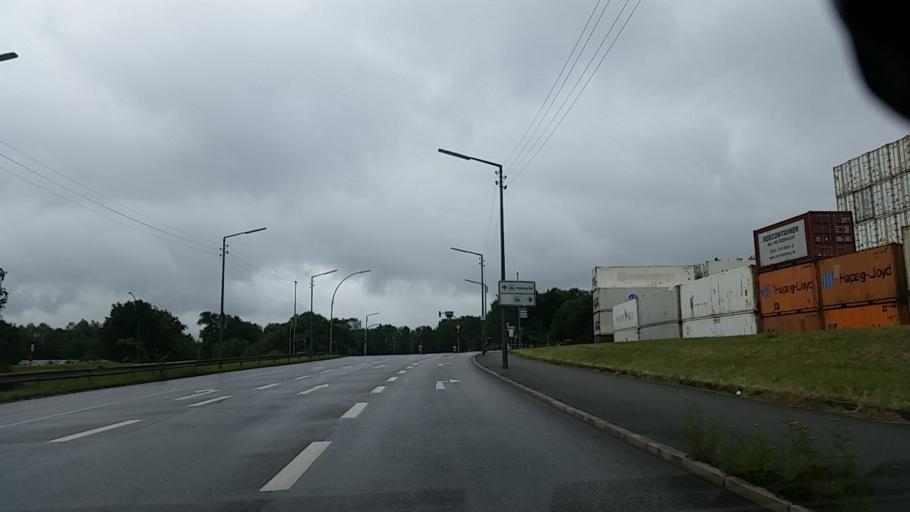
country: DE
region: Hamburg
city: Kleiner Grasbrook
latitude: 53.5124
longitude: 9.9777
